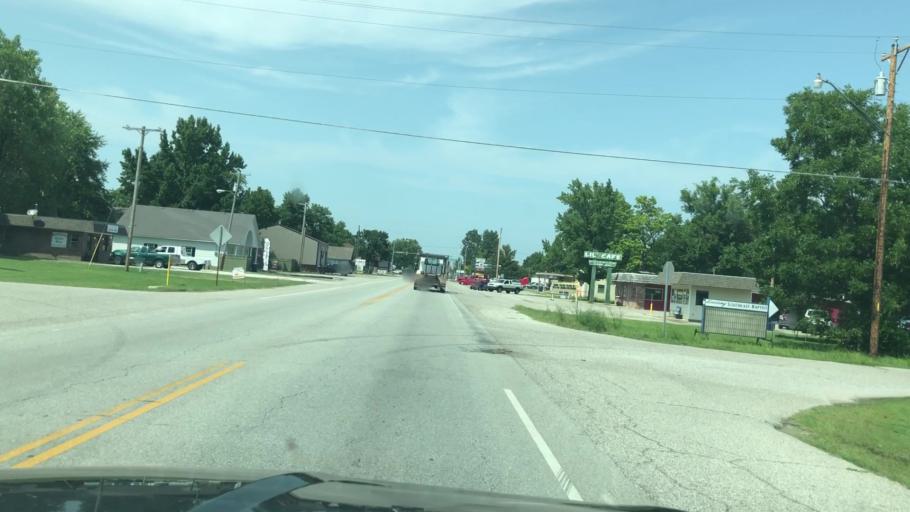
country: US
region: Oklahoma
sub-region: Ottawa County
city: Commerce
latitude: 36.9311
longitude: -94.8674
